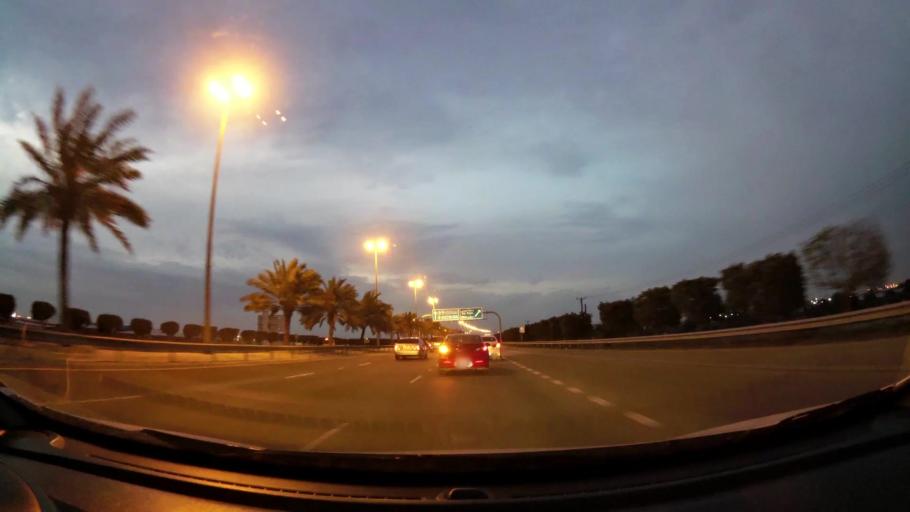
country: BH
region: Northern
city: Madinat `Isa
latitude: 26.1699
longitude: 50.5030
